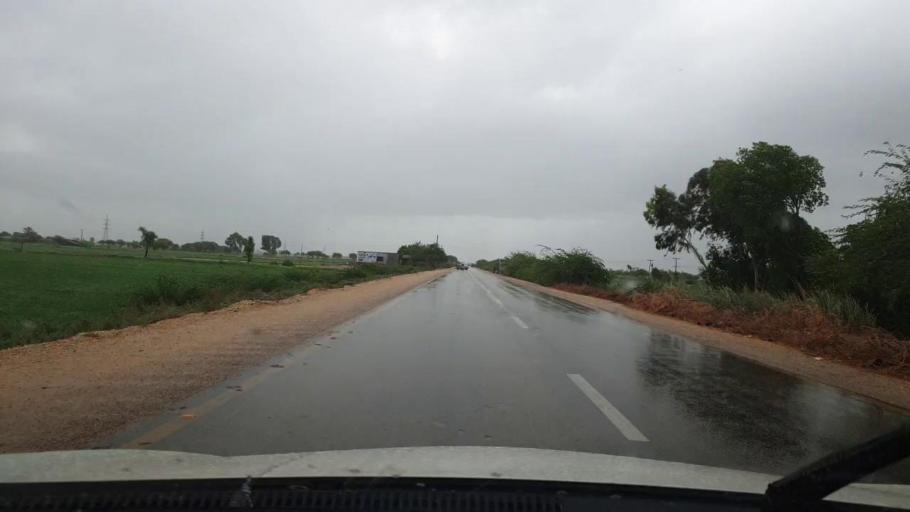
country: PK
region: Sindh
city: Kario
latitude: 24.6534
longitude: 68.5766
